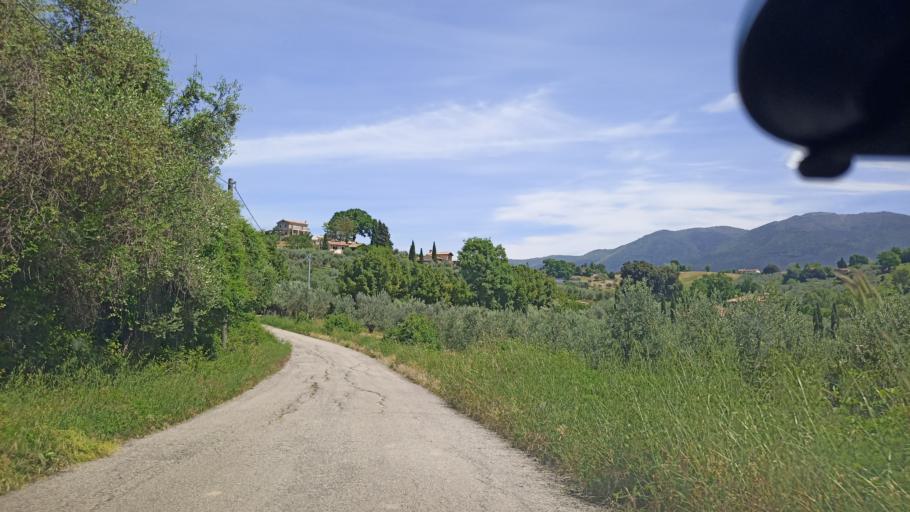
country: IT
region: Latium
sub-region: Provincia di Rieti
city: Torri in Sabina
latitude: 42.3552
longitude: 12.6342
